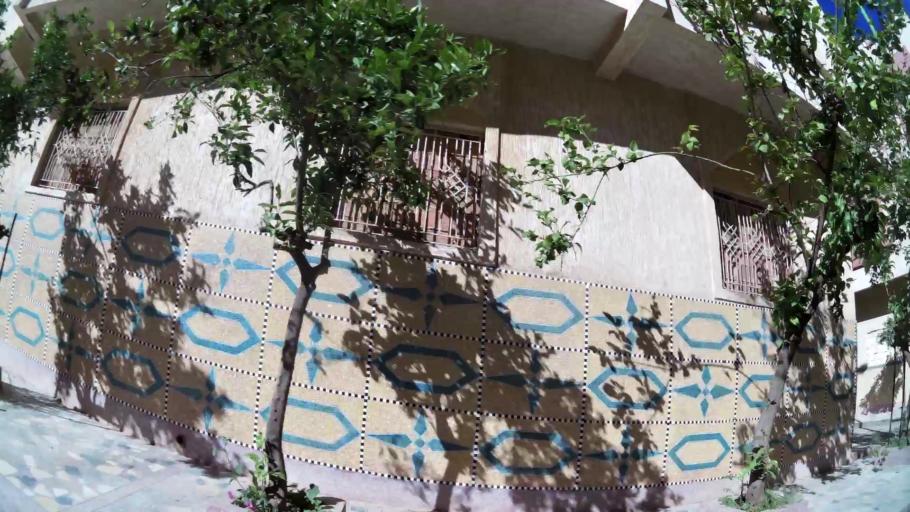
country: MA
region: Meknes-Tafilalet
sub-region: Meknes
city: Meknes
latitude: 33.8776
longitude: -5.5802
